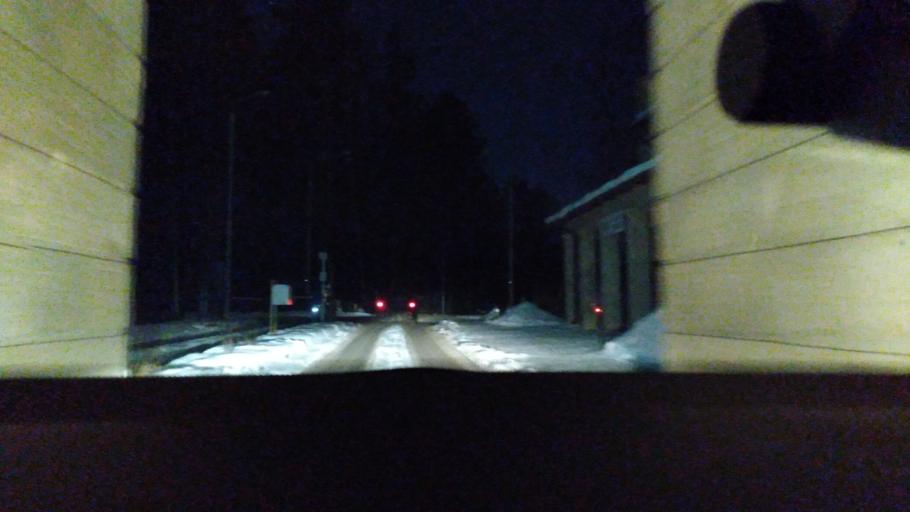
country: RU
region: Moskovskaya
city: Opalikha
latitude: 55.8119
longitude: 37.2458
